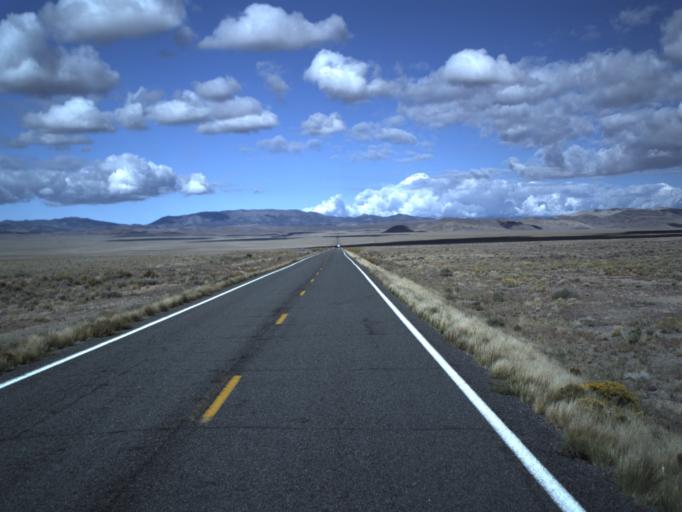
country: US
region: Utah
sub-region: Beaver County
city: Milford
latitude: 38.5365
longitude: -113.6931
